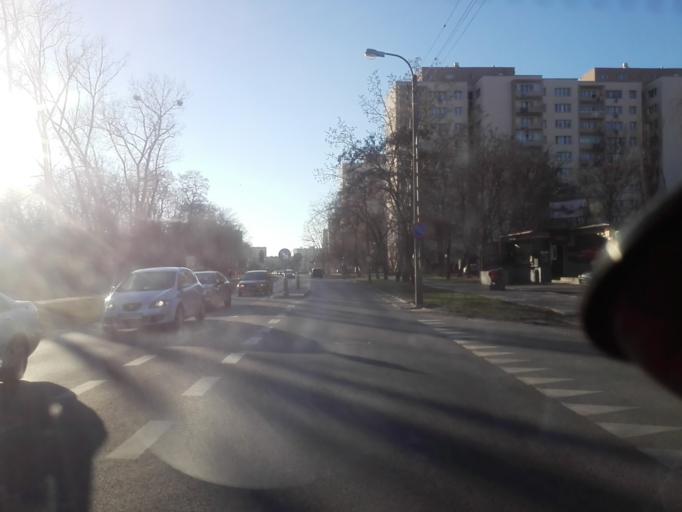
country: PL
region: Masovian Voivodeship
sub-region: Warszawa
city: Mokotow
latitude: 52.1738
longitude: 21.0172
